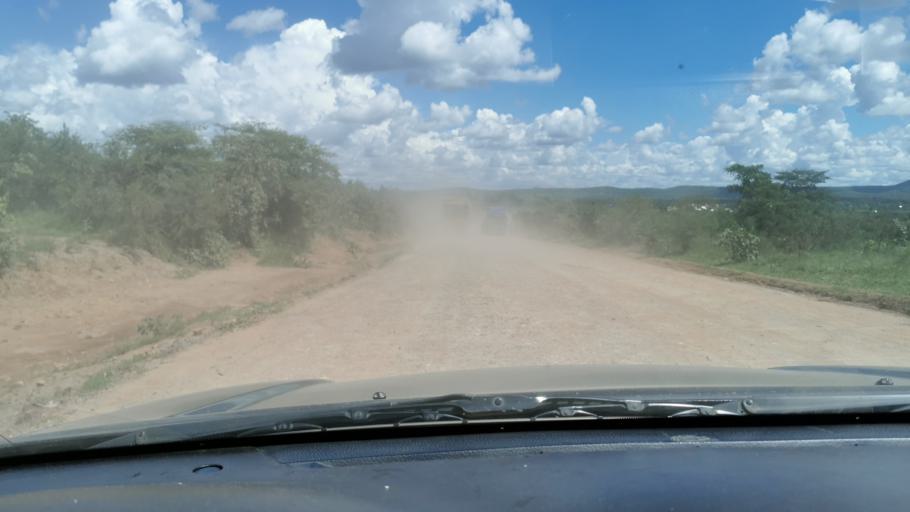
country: TZ
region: Kagera
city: Biharamulo
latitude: -2.9050
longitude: 31.1898
